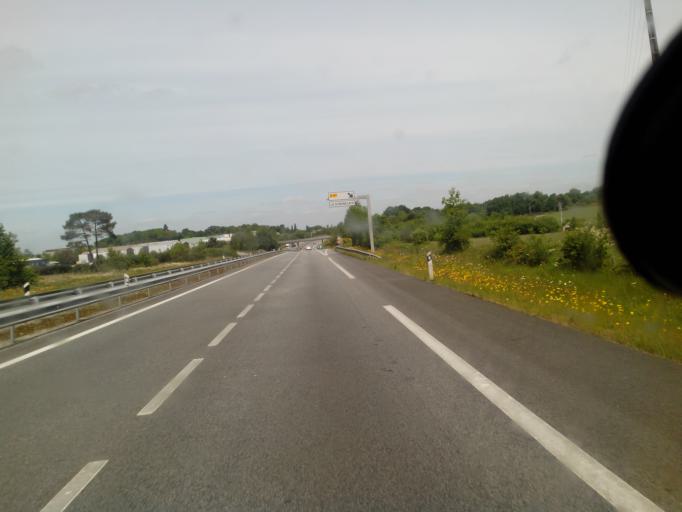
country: FR
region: Brittany
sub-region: Departement d'Ille-et-Vilaine
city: Grand-Fougeray
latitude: 47.7419
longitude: -1.7141
